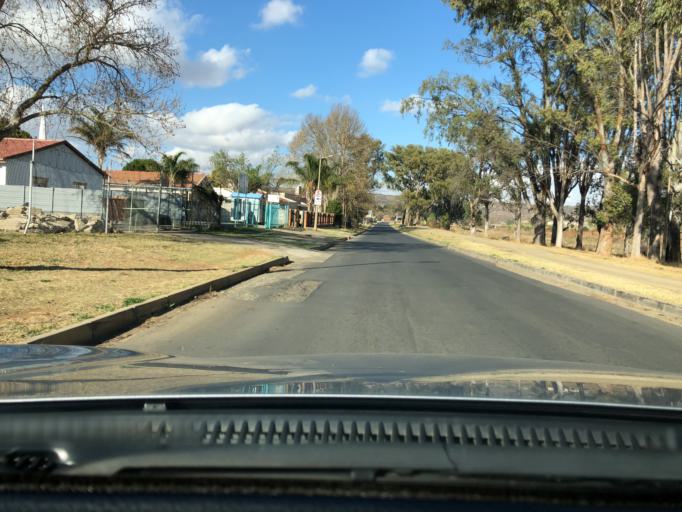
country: ZA
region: KwaZulu-Natal
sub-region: uThukela District Municipality
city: Ladysmith
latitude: -28.5618
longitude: 29.7777
